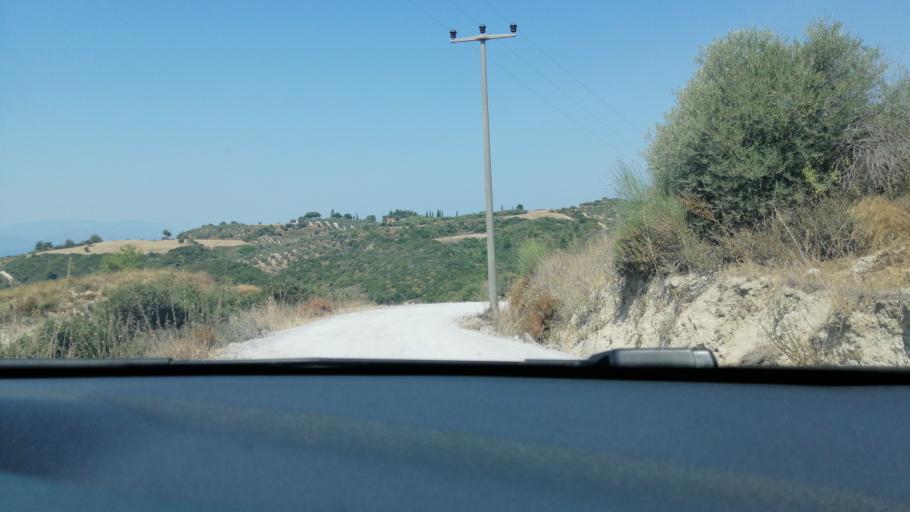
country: TR
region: Aydin
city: Davutlar
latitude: 37.7801
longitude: 27.3140
